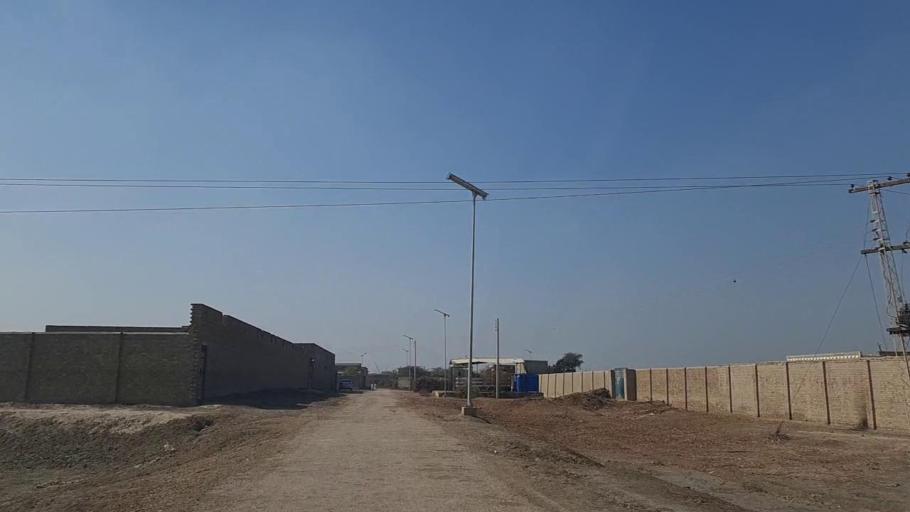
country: PK
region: Sindh
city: Shahpur Chakar
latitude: 26.1945
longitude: 68.5541
